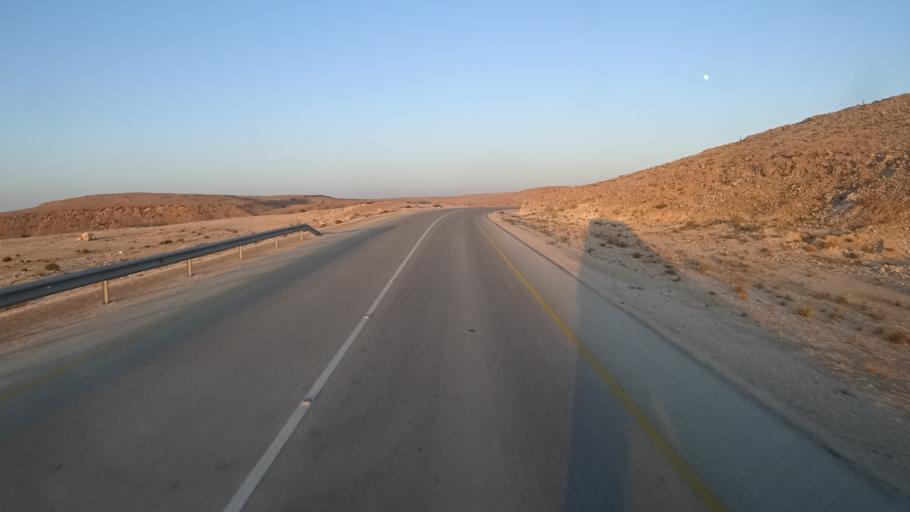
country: YE
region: Al Mahrah
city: Hawf
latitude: 16.9547
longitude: 53.3282
